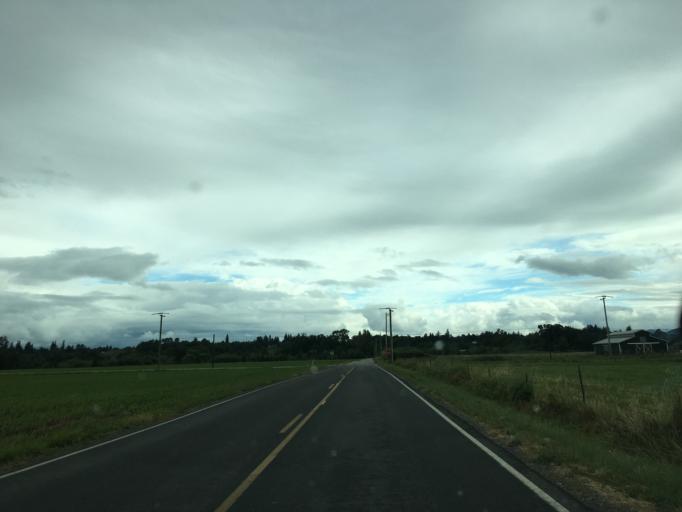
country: US
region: Washington
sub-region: Whatcom County
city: Sumas
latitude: 48.9775
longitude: -122.3089
